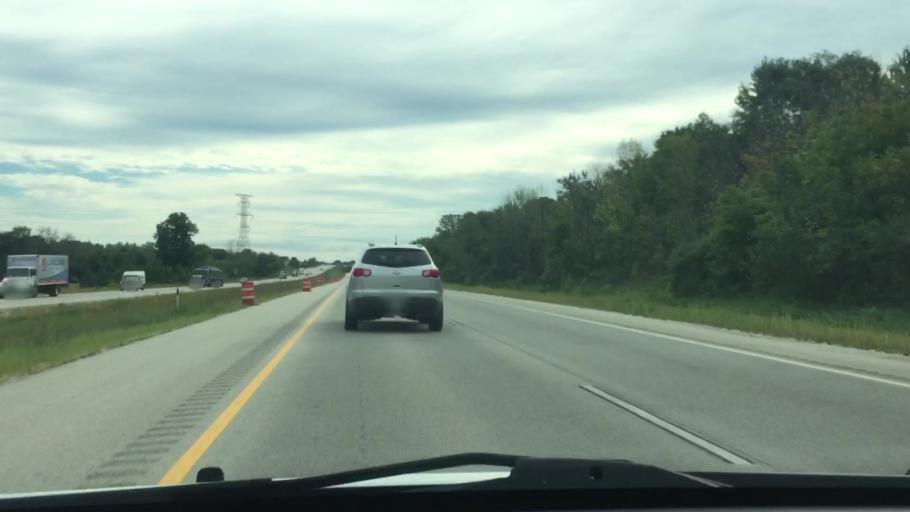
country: US
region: Wisconsin
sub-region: Waukesha County
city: Big Bend
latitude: 42.9074
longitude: -88.2281
